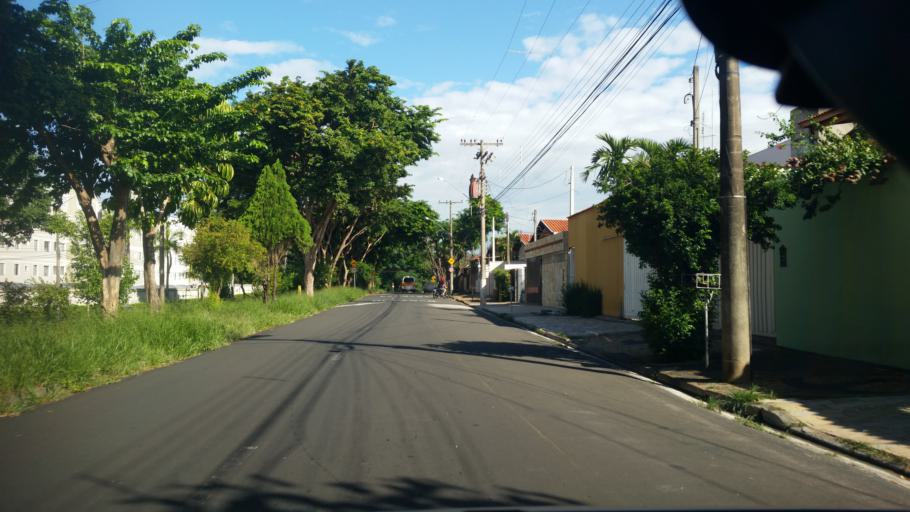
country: BR
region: Sao Paulo
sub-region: Campinas
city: Campinas
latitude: -22.8839
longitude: -47.0281
